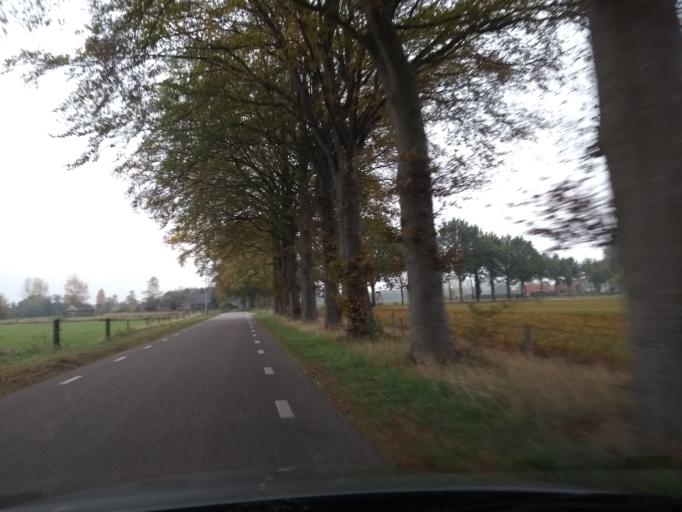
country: NL
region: Gelderland
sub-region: Gemeente Bronckhorst
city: Hengelo
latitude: 52.0463
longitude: 6.3220
